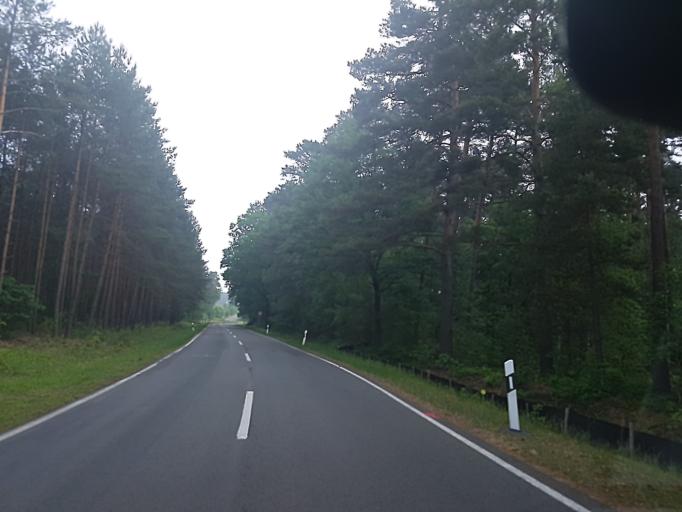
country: DE
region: Brandenburg
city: Gorzke
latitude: 52.0897
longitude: 12.3331
